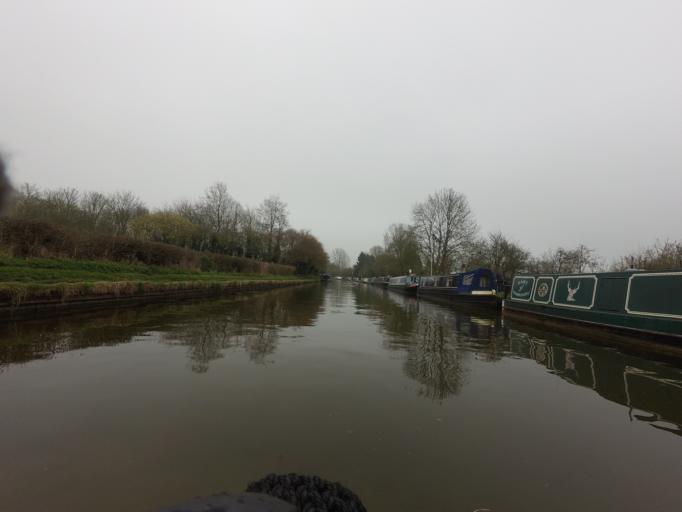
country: GB
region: England
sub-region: Hertfordshire
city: Tring
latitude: 51.7861
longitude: -0.6151
